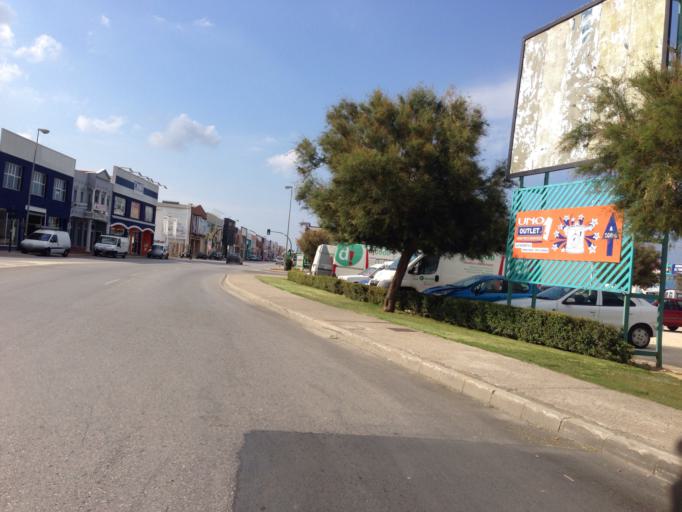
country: ES
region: Andalusia
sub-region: Provincia de Cadiz
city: Chiclana de la Frontera
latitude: 36.4293
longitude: -6.1508
